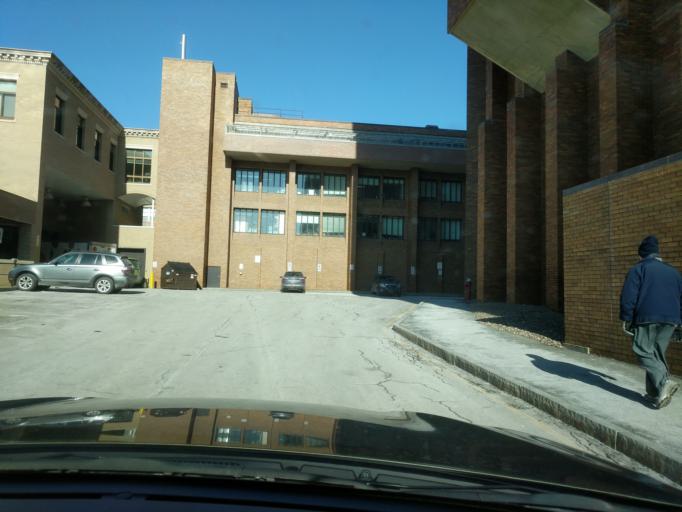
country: US
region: New York
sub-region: Tompkins County
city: East Ithaca
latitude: 42.4479
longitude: -76.4761
